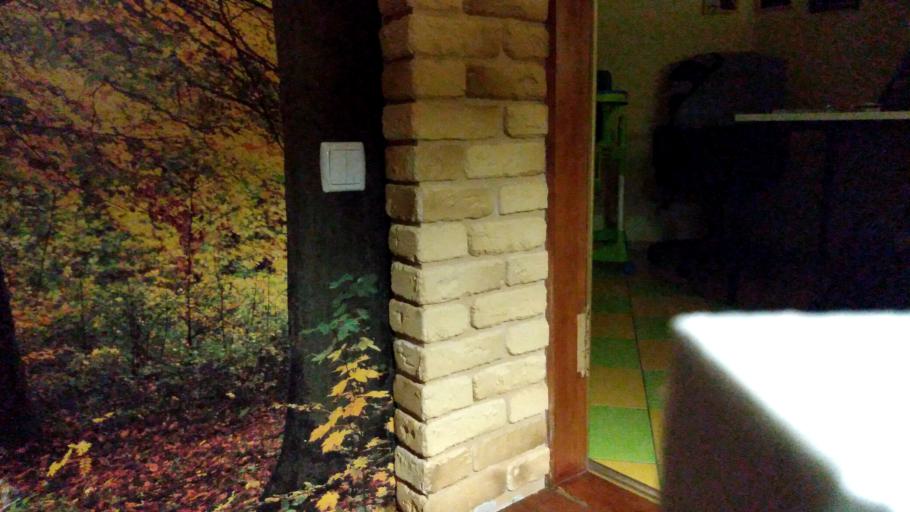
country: RU
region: Vologda
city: Lipin Bor
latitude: 61.0062
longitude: 37.9586
